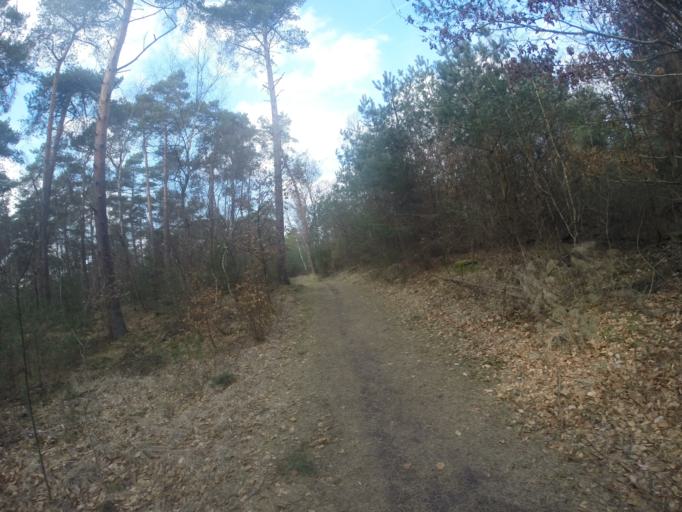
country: NL
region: Gelderland
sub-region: Gemeente Lochem
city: Almen
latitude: 52.1304
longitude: 6.3241
